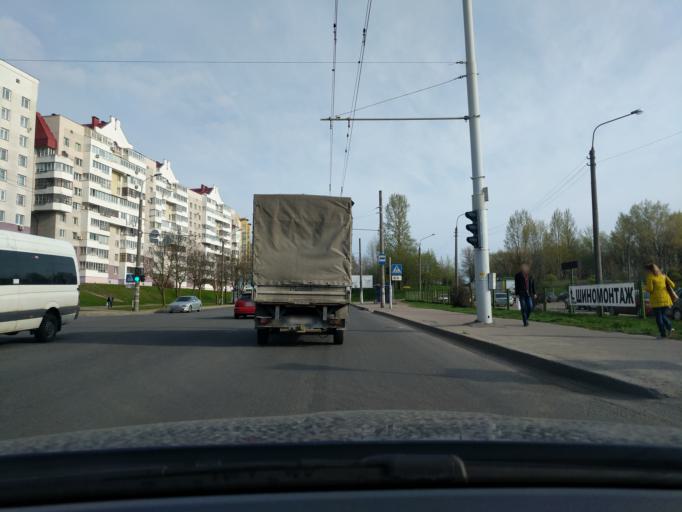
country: BY
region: Minsk
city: Novoye Medvezhino
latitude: 53.9038
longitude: 27.4631
